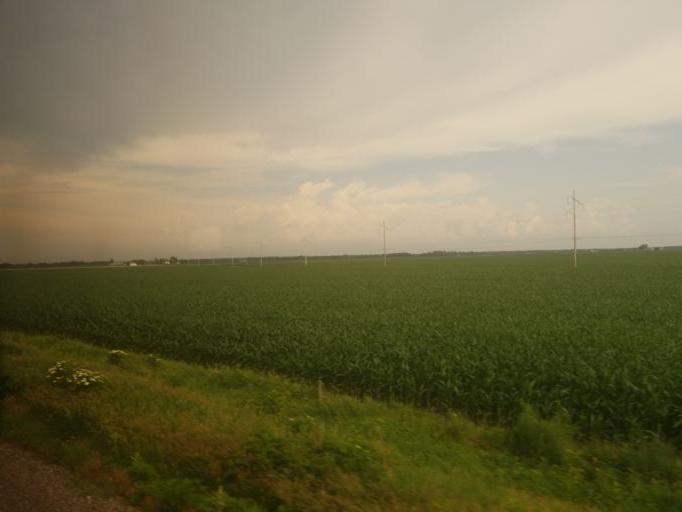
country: US
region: Illinois
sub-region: Bureau County
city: Princeton
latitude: 41.3806
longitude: -89.5384
